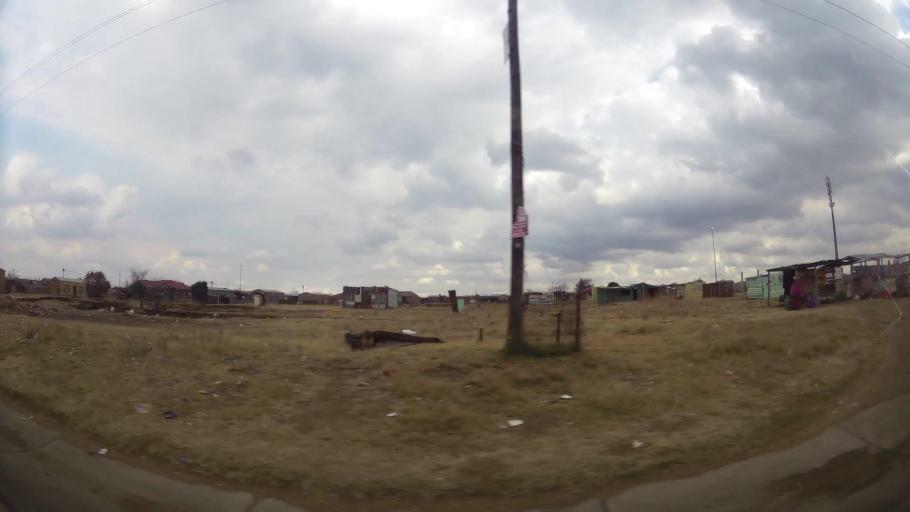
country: ZA
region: Orange Free State
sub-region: Fezile Dabi District Municipality
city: Sasolburg
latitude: -26.8549
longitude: 27.8765
